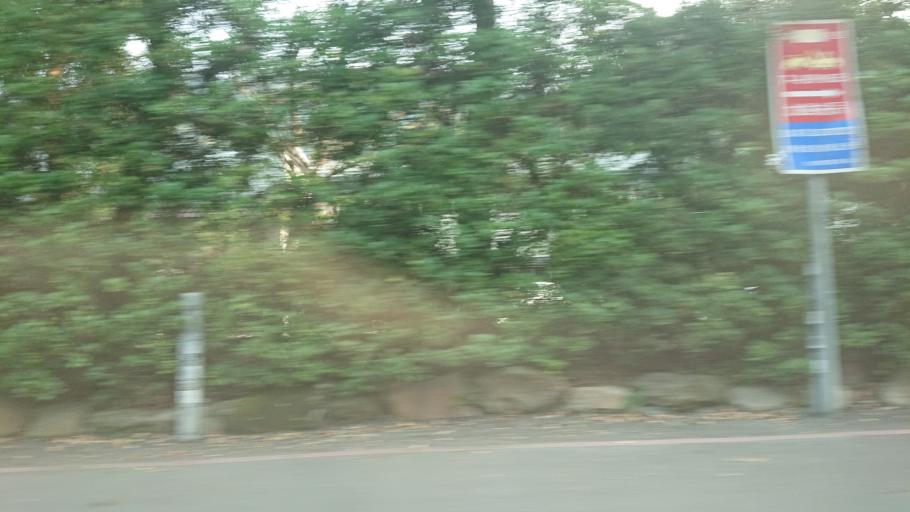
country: TW
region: Taiwan
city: Daxi
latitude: 24.8704
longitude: 121.4074
